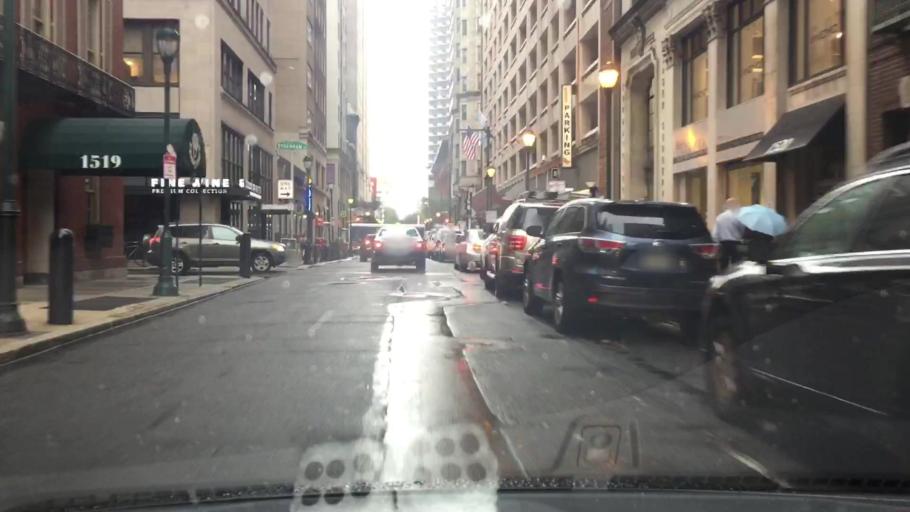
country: US
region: Pennsylvania
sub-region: Philadelphia County
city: Philadelphia
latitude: 39.9486
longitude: -75.1674
